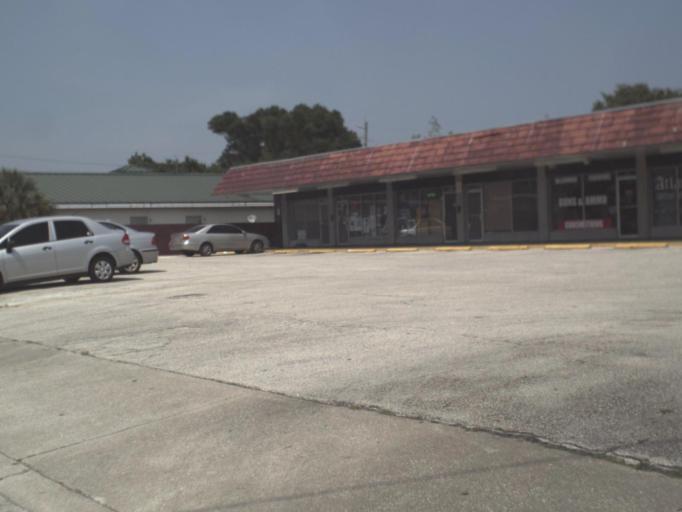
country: US
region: Florida
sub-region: Duval County
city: Atlantic Beach
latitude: 30.3337
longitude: -81.4155
